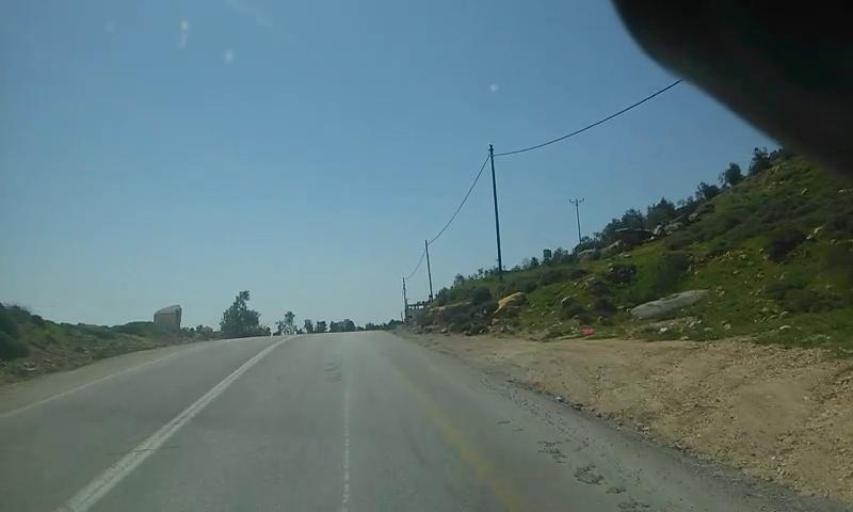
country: PS
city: Bayt `Amrah
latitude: 31.4760
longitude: 35.0434
